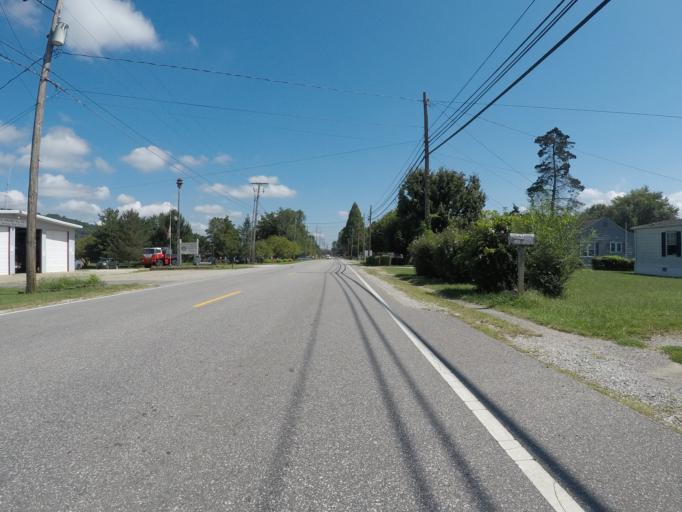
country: US
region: Ohio
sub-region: Lawrence County
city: Burlington
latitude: 38.4084
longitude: -82.5252
